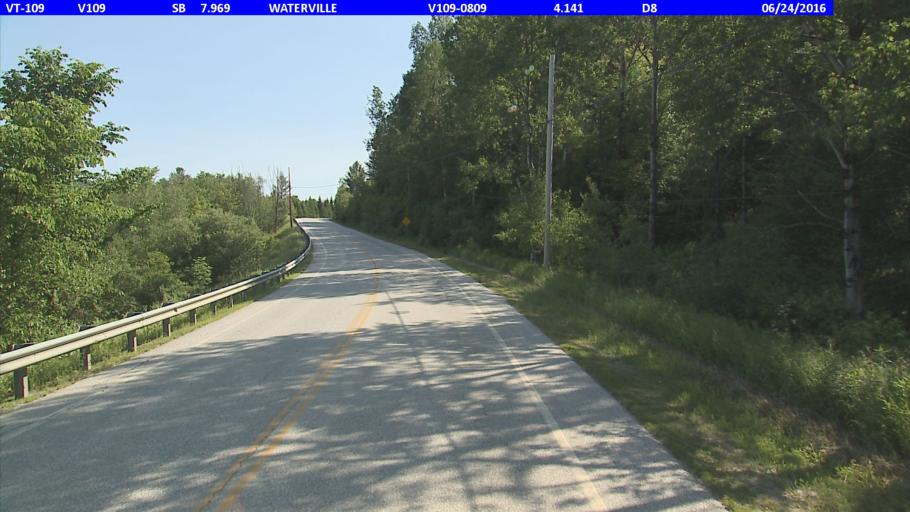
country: US
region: Vermont
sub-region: Lamoille County
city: Johnson
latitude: 44.7363
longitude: -72.7444
